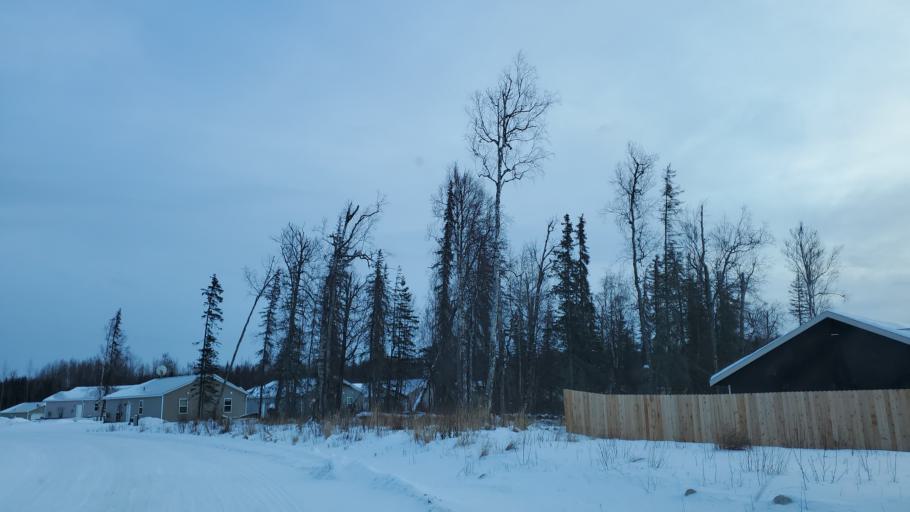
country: US
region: Alaska
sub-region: Matanuska-Susitna Borough
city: Fishhook
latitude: 61.6834
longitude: -149.2446
